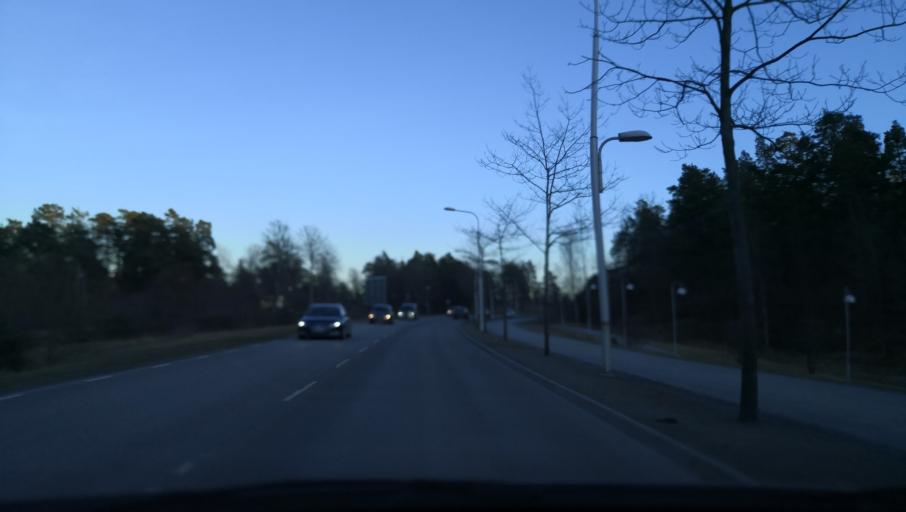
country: SE
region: Stockholm
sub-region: Varmdo Kommun
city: Gustavsberg
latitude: 59.3176
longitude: 18.3899
